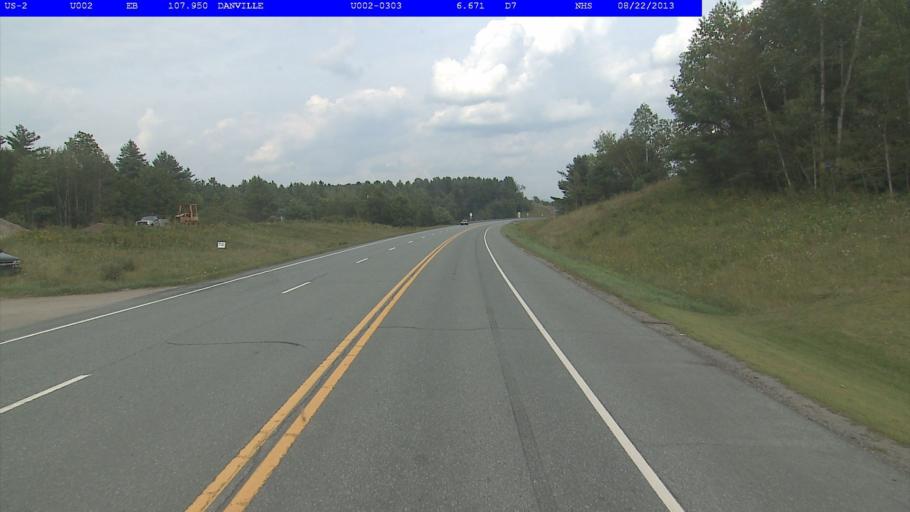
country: US
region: Vermont
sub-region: Caledonia County
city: St Johnsbury
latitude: 44.4294
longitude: -72.1037
